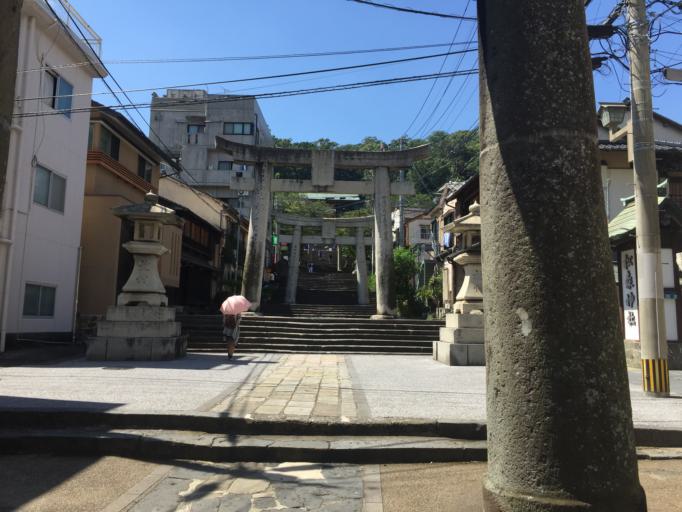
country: JP
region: Nagasaki
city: Nagasaki-shi
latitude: 32.7531
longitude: 129.8832
